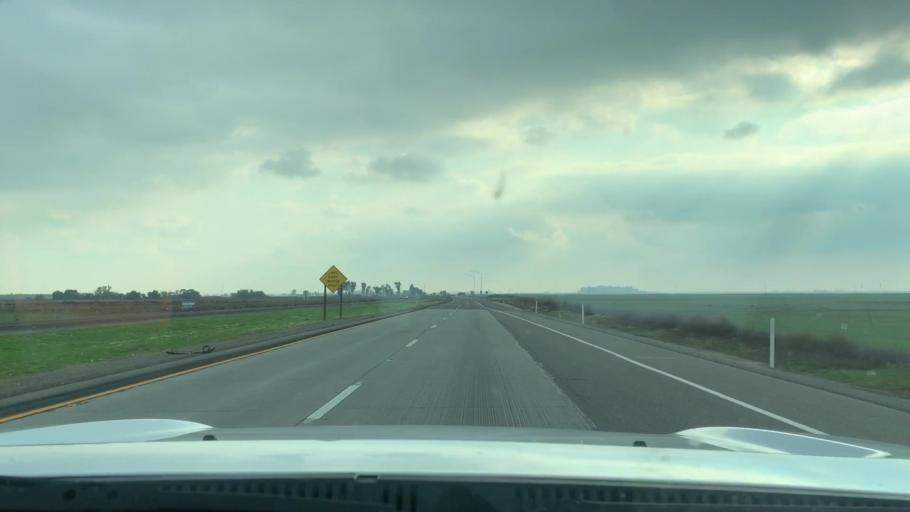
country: US
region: California
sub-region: Kings County
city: Lemoore
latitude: 36.2778
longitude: -119.8082
